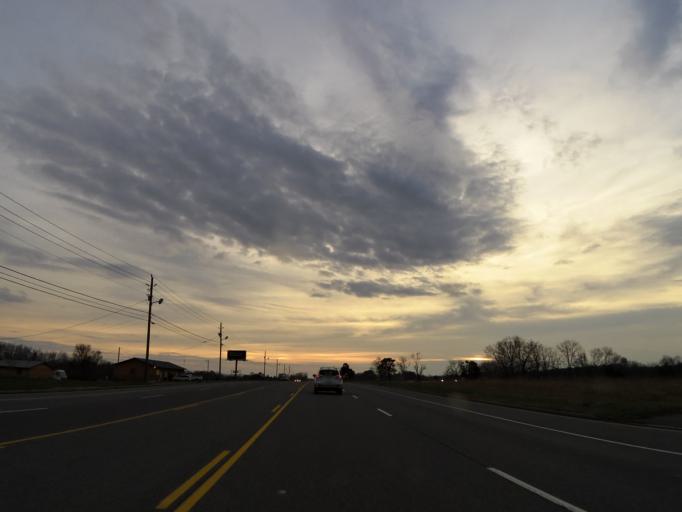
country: US
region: Tennessee
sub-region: Monroe County
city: Madisonville
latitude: 35.5005
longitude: -84.3840
